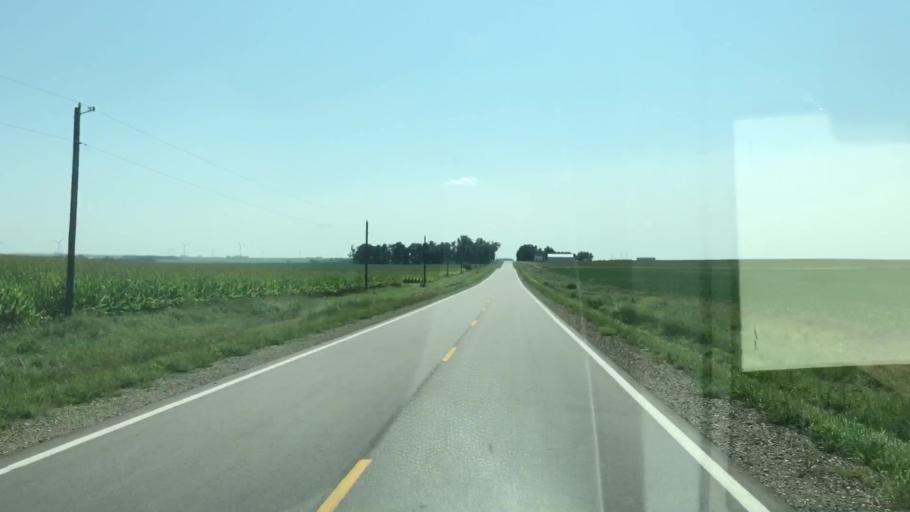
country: US
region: Iowa
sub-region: O'Brien County
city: Sanborn
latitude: 43.2686
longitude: -95.7236
